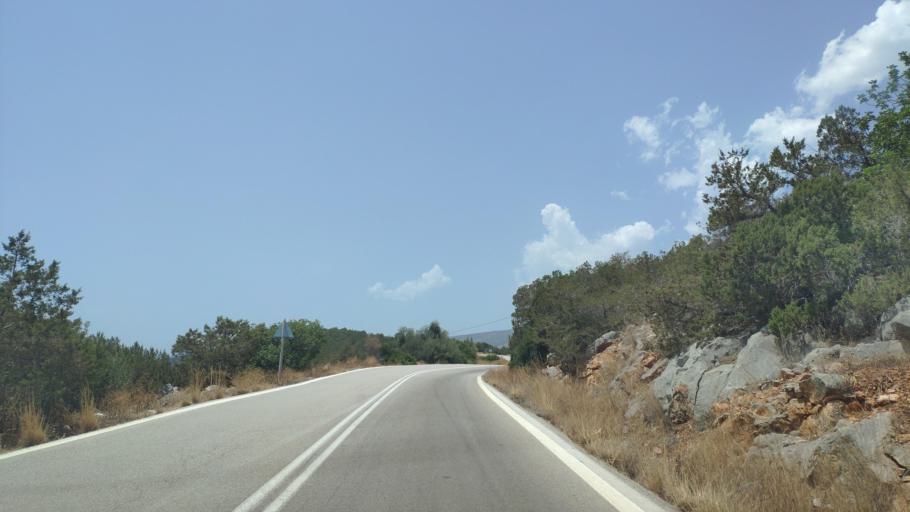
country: GR
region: Peloponnese
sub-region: Nomos Argolidos
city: Koilas
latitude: 37.4220
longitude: 23.1536
